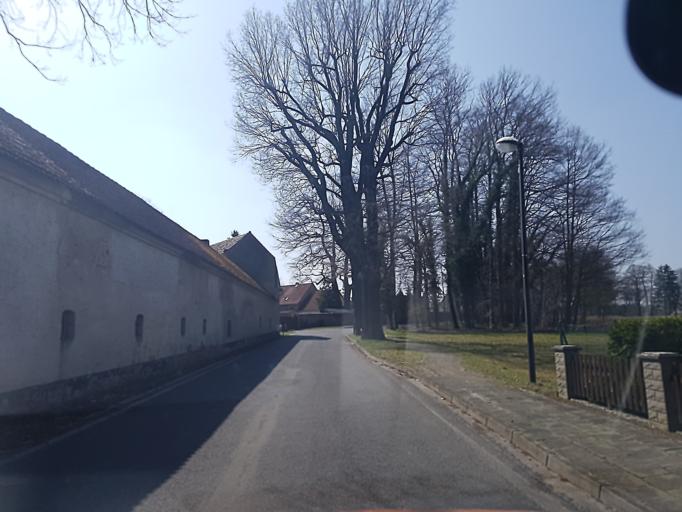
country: DE
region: Saxony
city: Gross Duben
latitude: 51.6778
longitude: 14.5401
